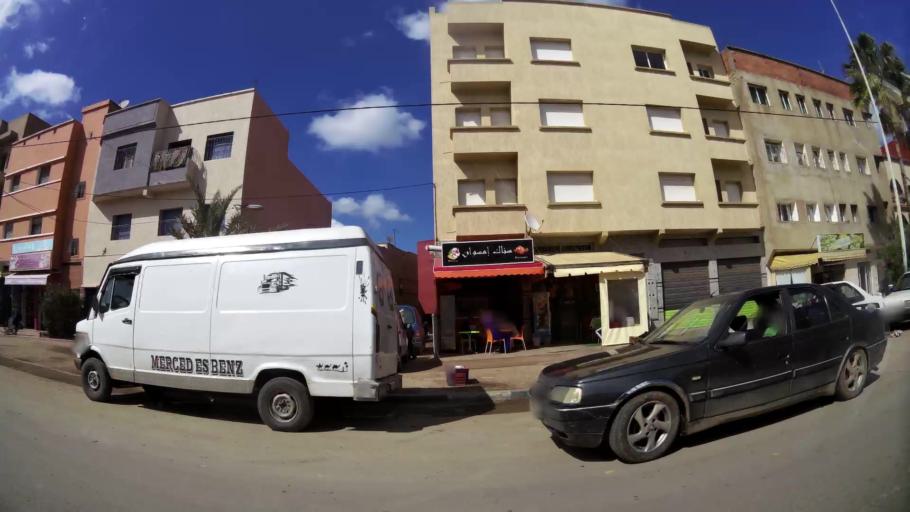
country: MA
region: Grand Casablanca
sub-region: Mediouna
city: Mediouna
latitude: 33.4521
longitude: -7.5134
